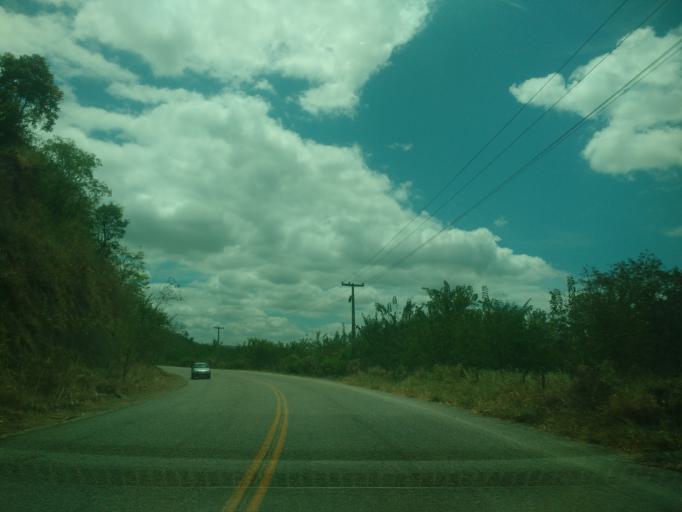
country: BR
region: Alagoas
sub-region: Santana Do Mundau
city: Santana do Mundau
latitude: -9.1456
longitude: -36.1705
